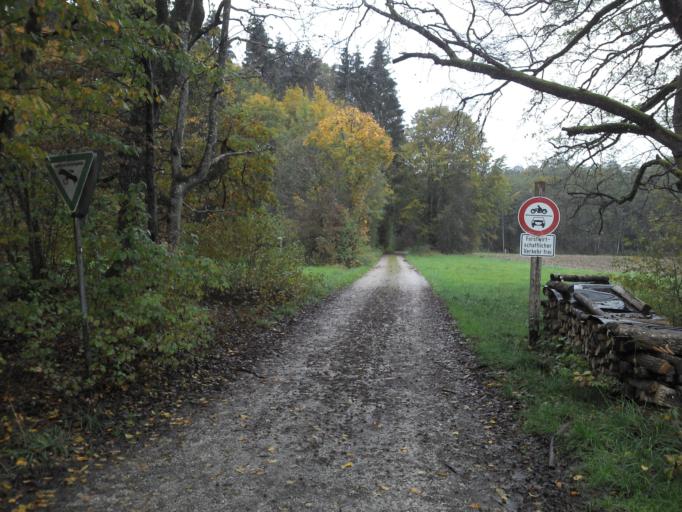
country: DE
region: Bavaria
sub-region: Upper Bavaria
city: Seeshaupt
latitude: 47.8186
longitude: 11.2825
